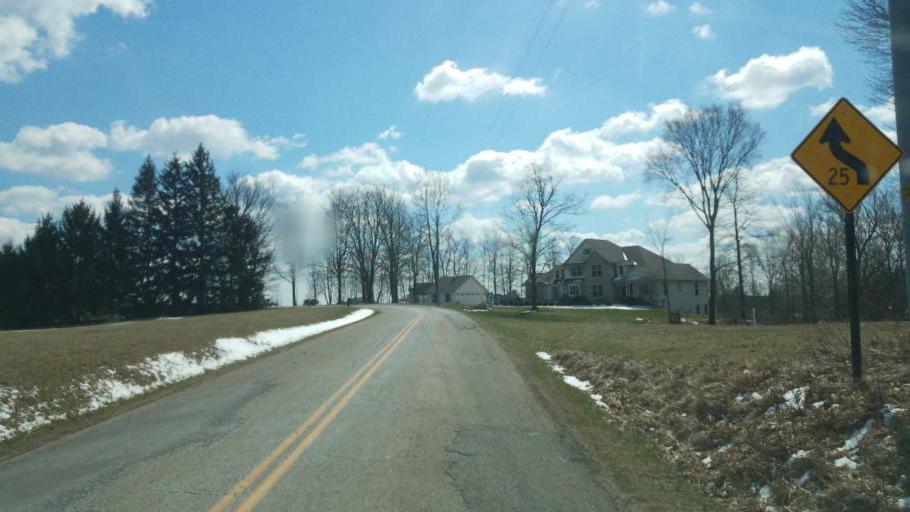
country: US
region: Ohio
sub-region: Knox County
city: Mount Vernon
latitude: 40.3418
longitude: -82.5487
